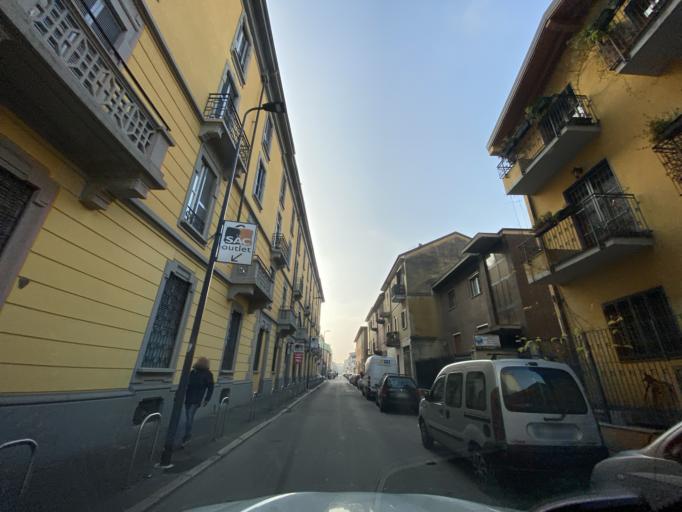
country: IT
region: Lombardy
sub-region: Citta metropolitana di Milano
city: Bresso
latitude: 45.5042
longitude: 9.1749
